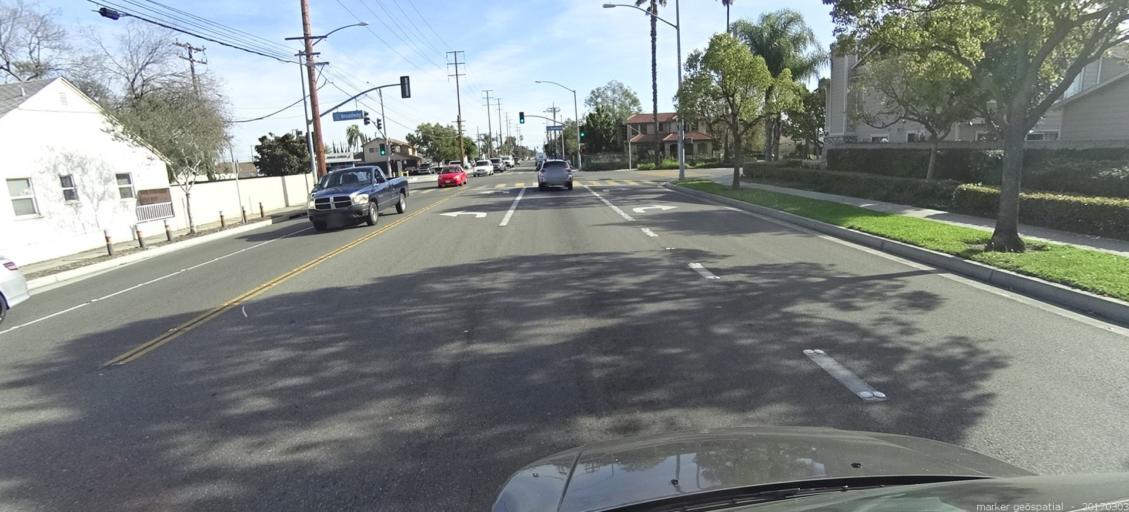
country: US
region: California
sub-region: Orange County
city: Anaheim
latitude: 33.8364
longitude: -117.9022
